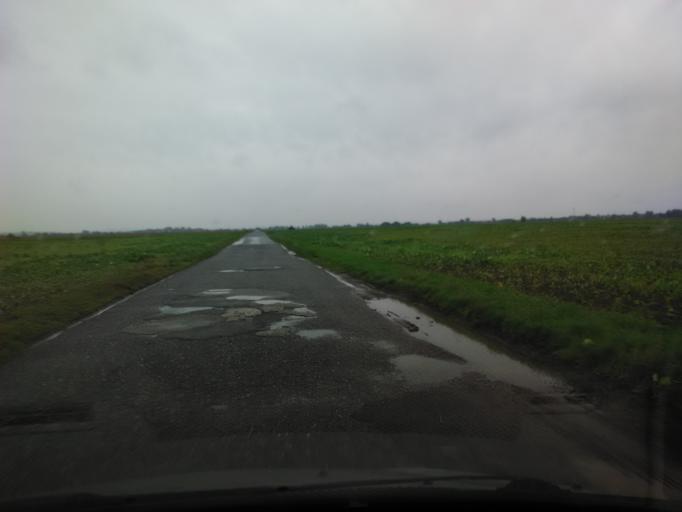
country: SK
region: Nitriansky
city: Tlmace
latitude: 48.2632
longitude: 18.5436
